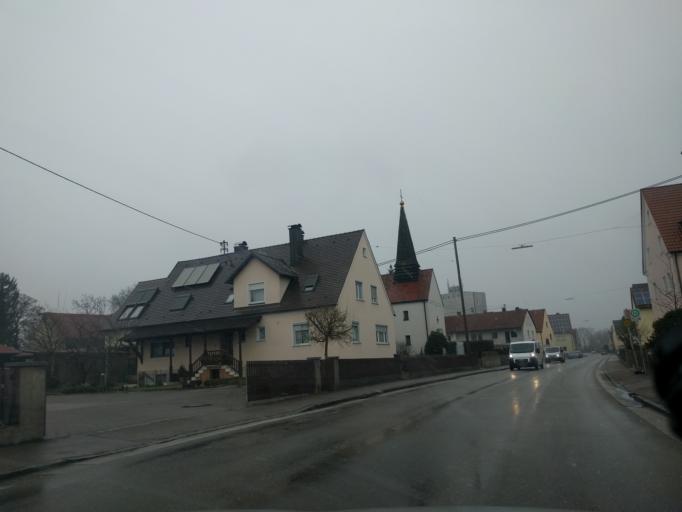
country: DE
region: Bavaria
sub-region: Swabia
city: Donauwoerth
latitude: 48.7016
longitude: 10.7970
